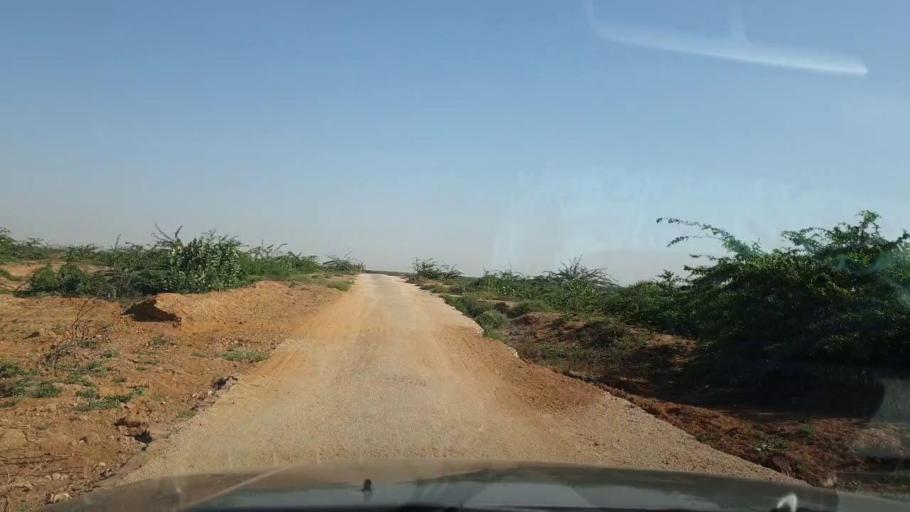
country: PK
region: Sindh
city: Thatta
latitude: 24.8844
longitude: 67.7985
